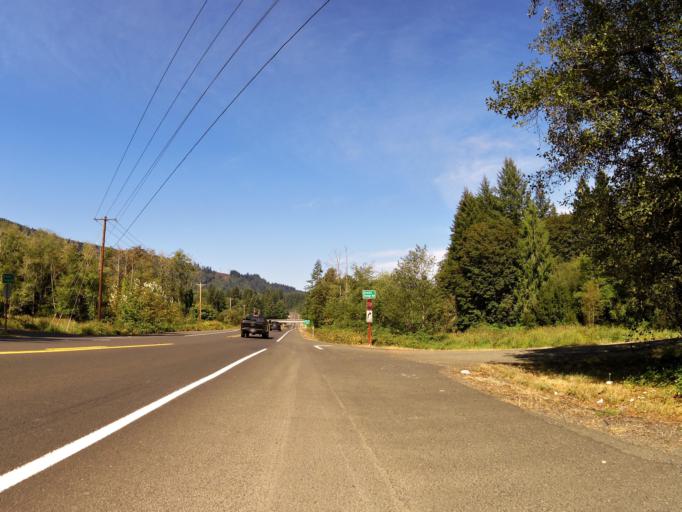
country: US
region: Washington
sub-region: Wahkiakum County
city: Cathlamet
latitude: 46.1474
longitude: -123.4037
